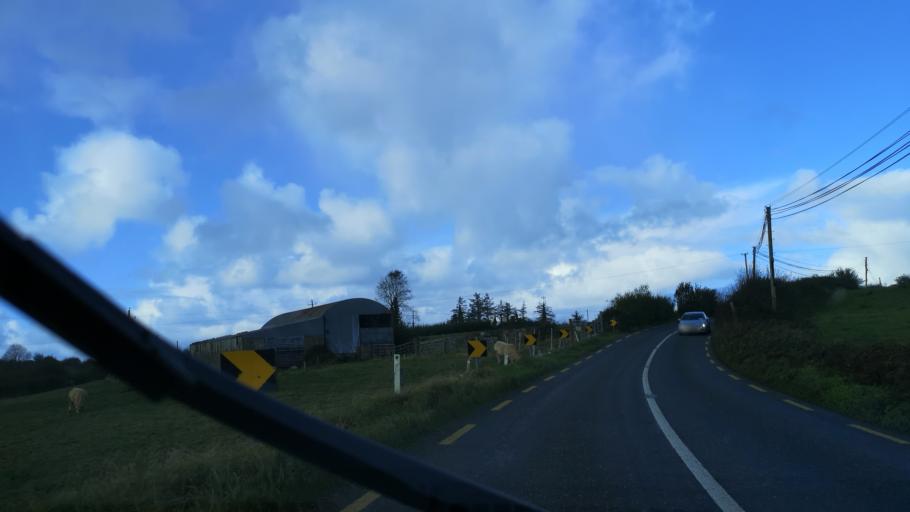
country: IE
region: Connaught
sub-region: Maigh Eo
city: Westport
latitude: 53.7762
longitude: -9.4146
